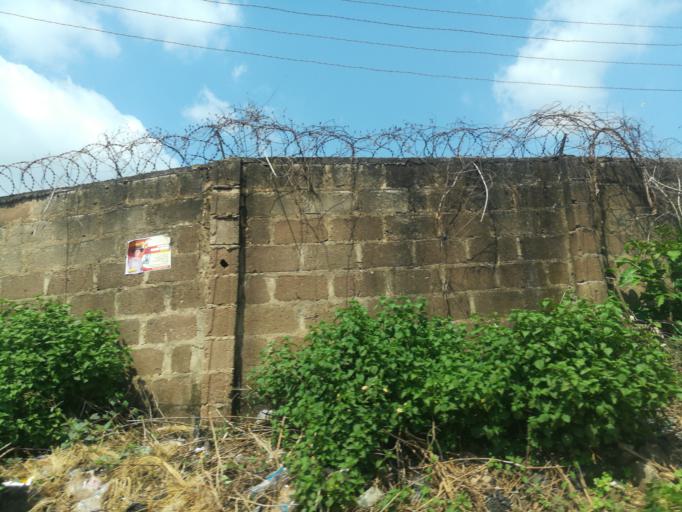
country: NG
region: Oyo
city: Moniya
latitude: 7.5020
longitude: 3.9137
